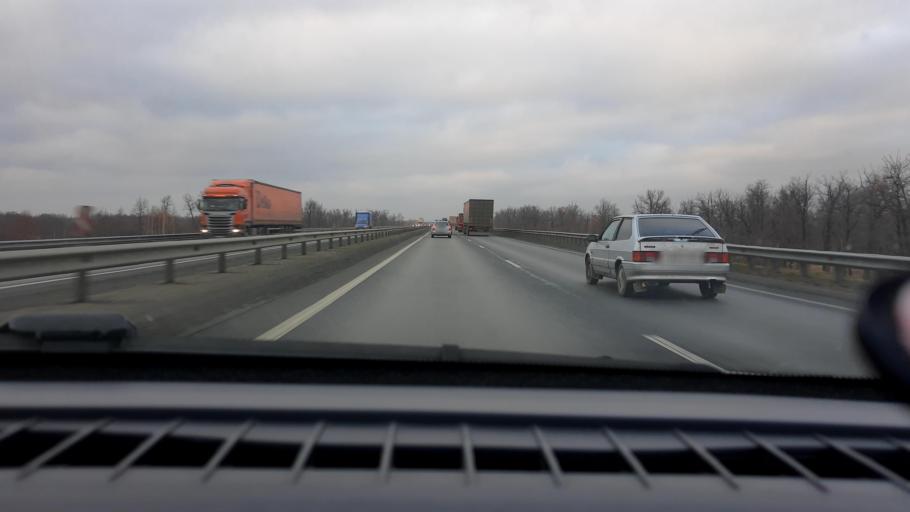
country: RU
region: Nizjnij Novgorod
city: Gorbatovka
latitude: 56.2024
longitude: 43.7525
